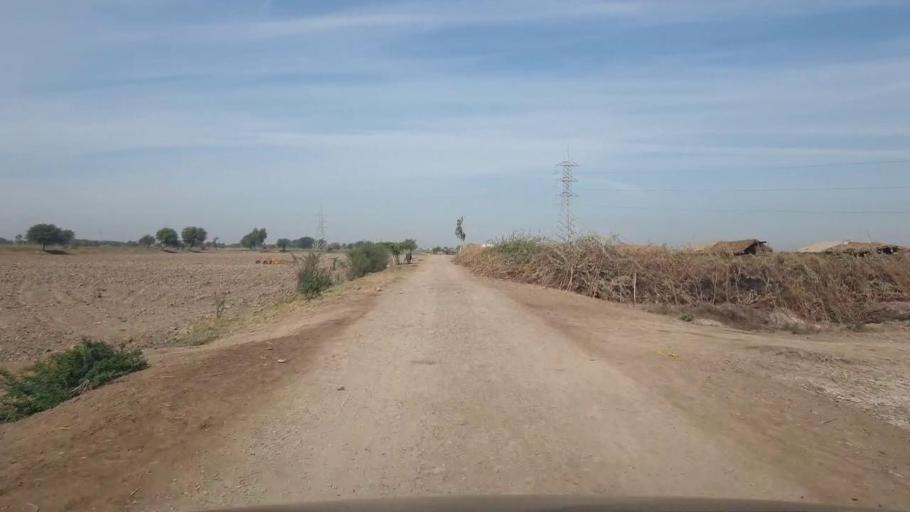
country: PK
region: Sindh
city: Umarkot
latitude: 25.3673
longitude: 69.6487
